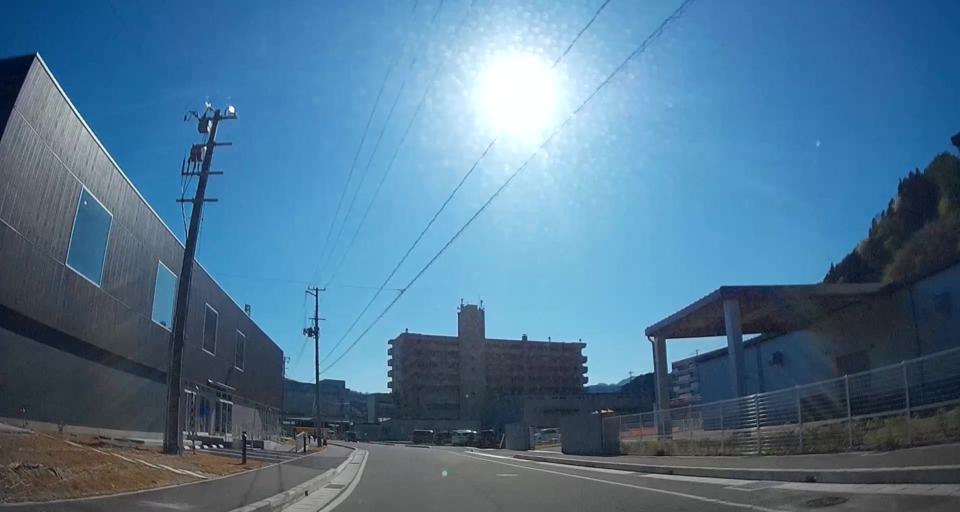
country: JP
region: Iwate
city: Kamaishi
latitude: 39.2747
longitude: 141.8900
